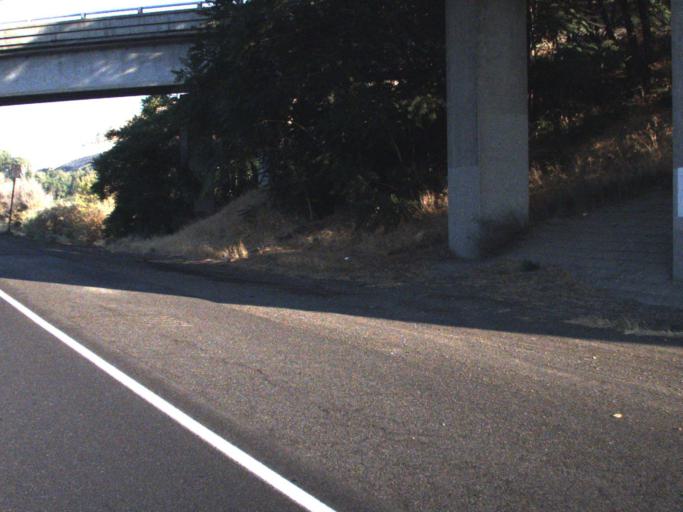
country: US
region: Washington
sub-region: Yakima County
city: Yakima
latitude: 46.6265
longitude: -120.5076
